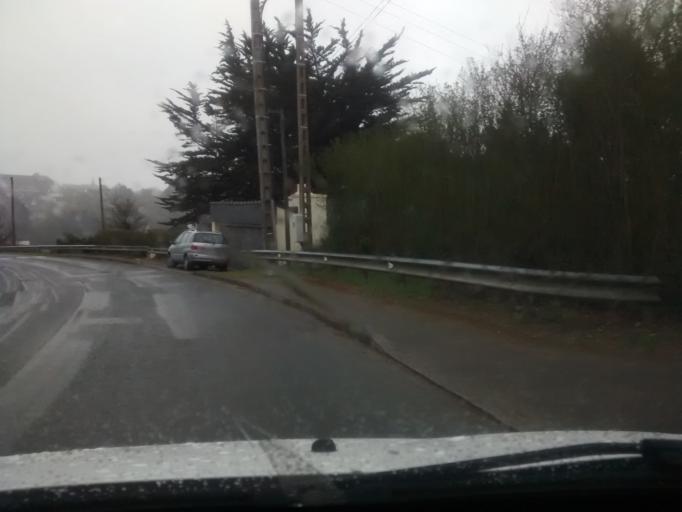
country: FR
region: Brittany
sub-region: Departement des Cotes-d'Armor
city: Plouguiel
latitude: 48.7925
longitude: -3.2362
